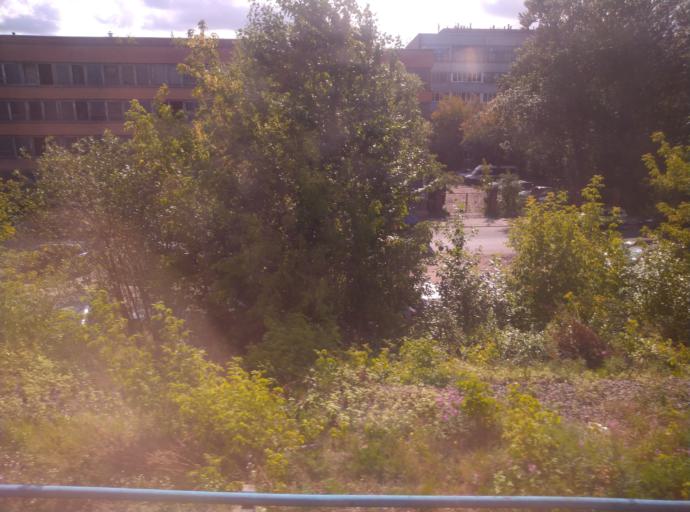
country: RU
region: St.-Petersburg
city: Centralniy
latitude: 59.9108
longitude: 30.3938
